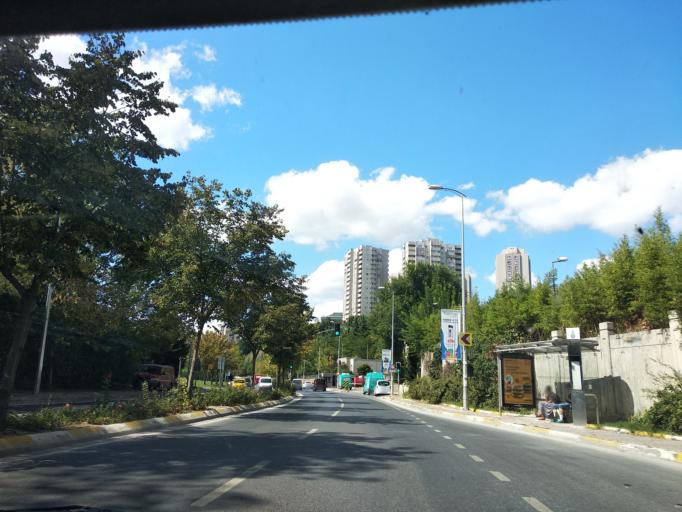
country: TR
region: Istanbul
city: Umraniye
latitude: 41.0057
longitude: 29.1121
